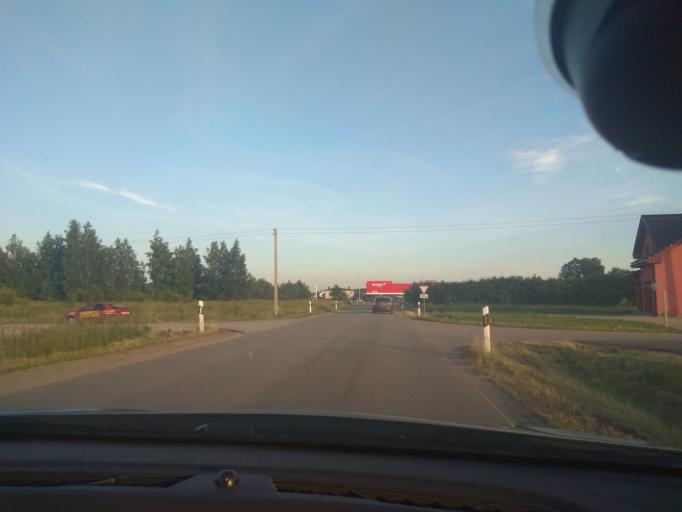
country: LT
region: Klaipedos apskritis
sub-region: Klaipeda
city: Klaipeda
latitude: 55.7544
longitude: 21.1743
